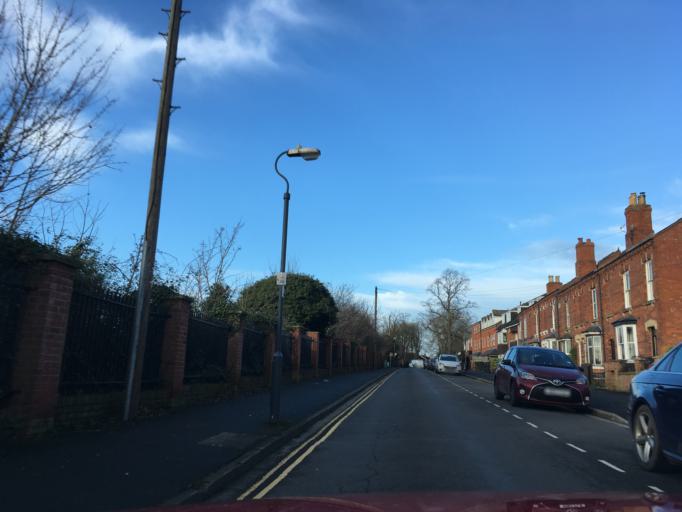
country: GB
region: England
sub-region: Warwickshire
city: Stratford-upon-Avon
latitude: 52.2002
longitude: -1.7098
